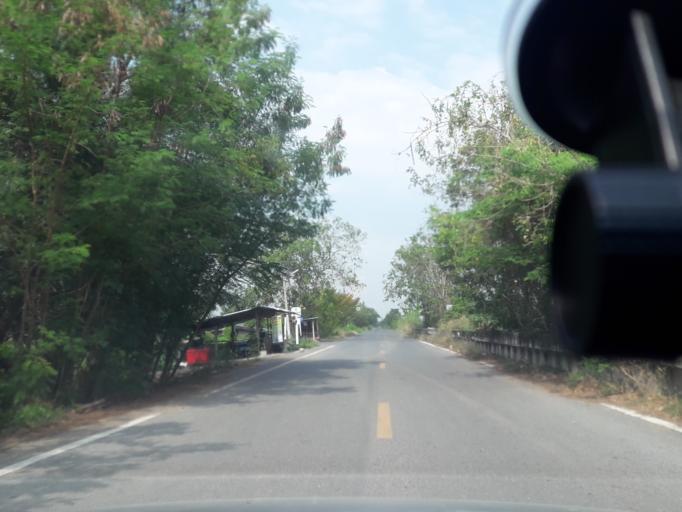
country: TH
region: Pathum Thani
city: Nong Suea
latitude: 14.2264
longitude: 100.8914
